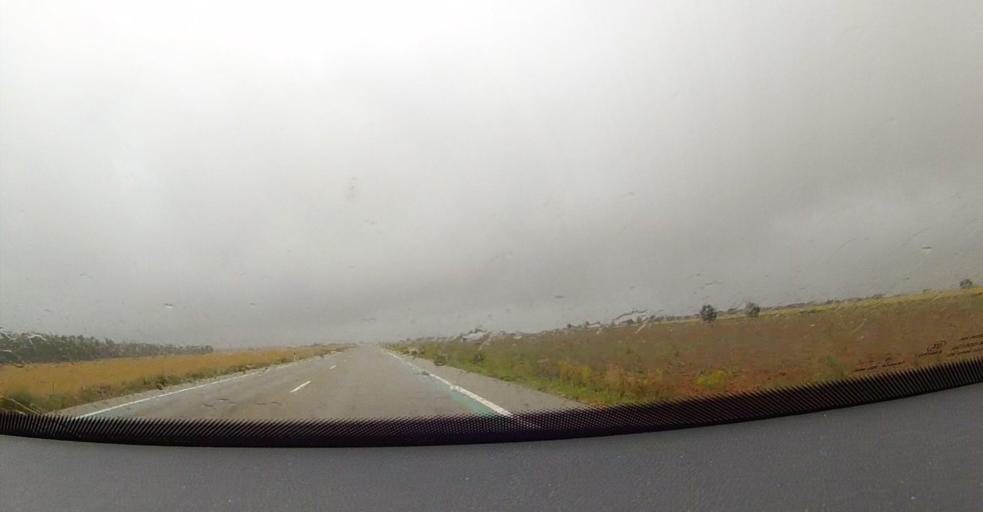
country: ES
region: Castille and Leon
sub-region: Provincia de Palencia
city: Poza de la Vega
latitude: 42.5986
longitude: -4.7632
